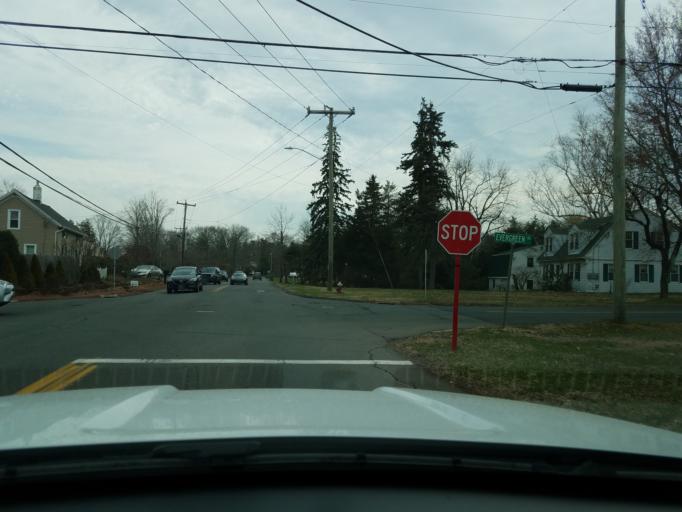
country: US
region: Connecticut
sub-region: Middlesex County
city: Cromwell
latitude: 41.6105
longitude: -72.6669
